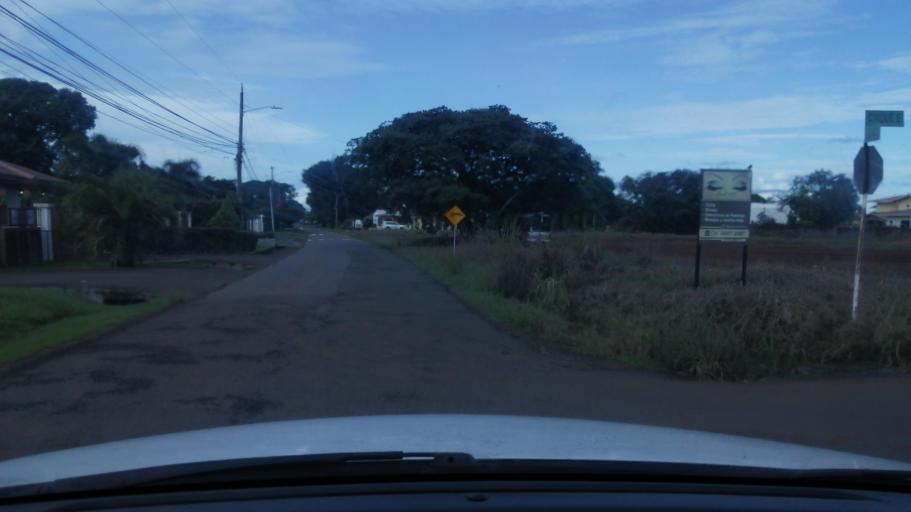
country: PA
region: Chiriqui
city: El Quiteno
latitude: 8.4602
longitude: -82.4177
